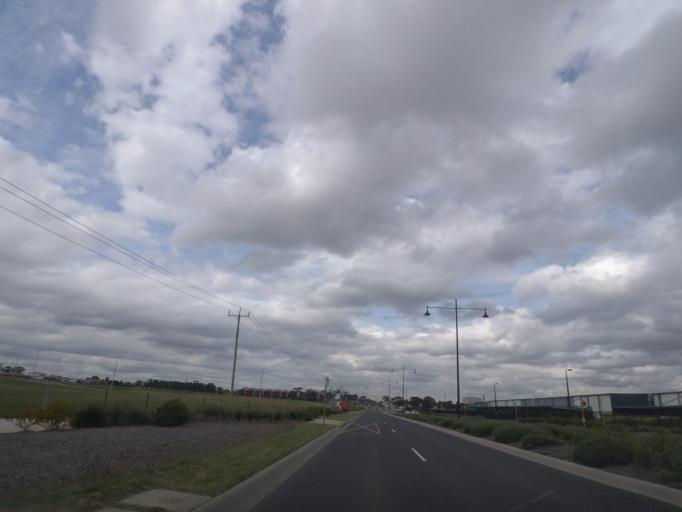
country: AU
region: Victoria
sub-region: Hume
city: Tullamarine
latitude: -37.6927
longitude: 144.8623
